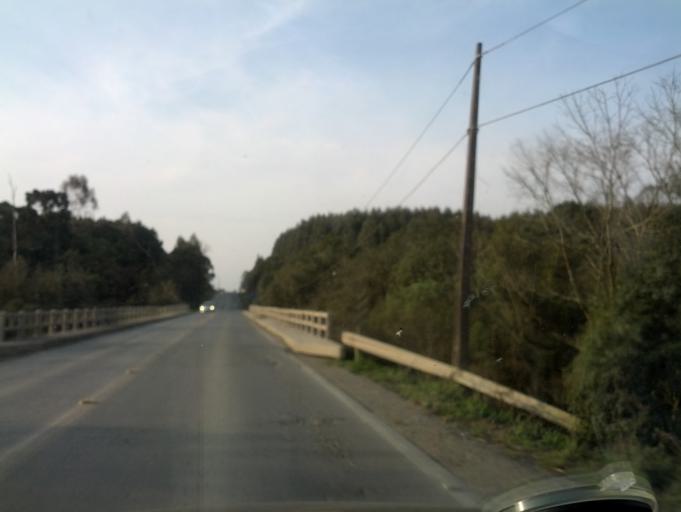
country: BR
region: Santa Catarina
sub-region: Otacilio Costa
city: Otacilio Costa
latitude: -27.5160
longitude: -50.1327
